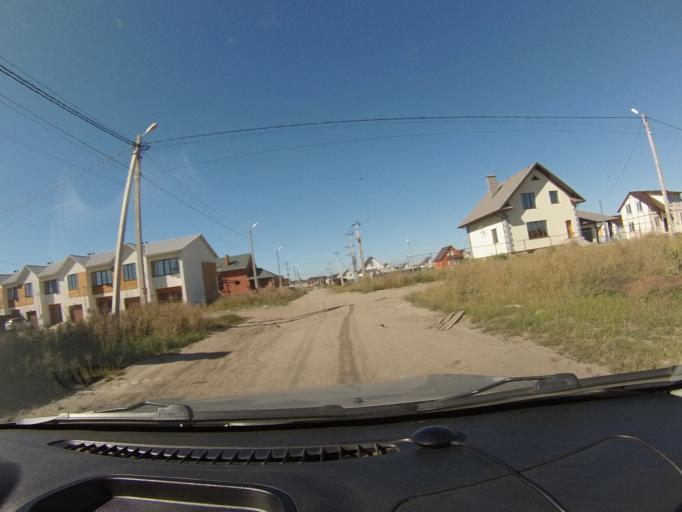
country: RU
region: Tambov
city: Komsomolets
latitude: 52.7785
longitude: 41.3710
